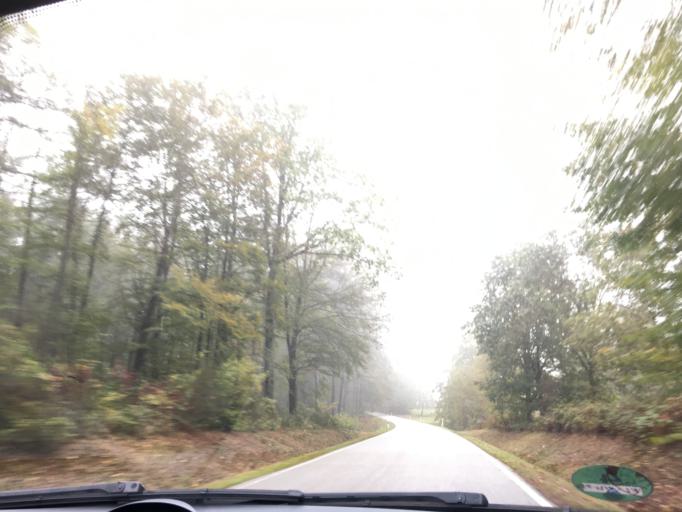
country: DE
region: Rheinland-Pfalz
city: Schmalenberg
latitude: 49.3196
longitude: 7.7593
